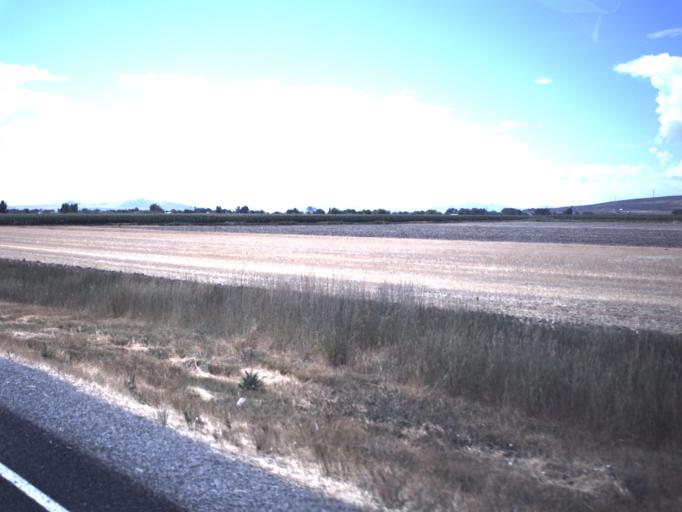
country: US
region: Utah
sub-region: Box Elder County
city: Garland
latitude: 41.7680
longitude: -112.1489
